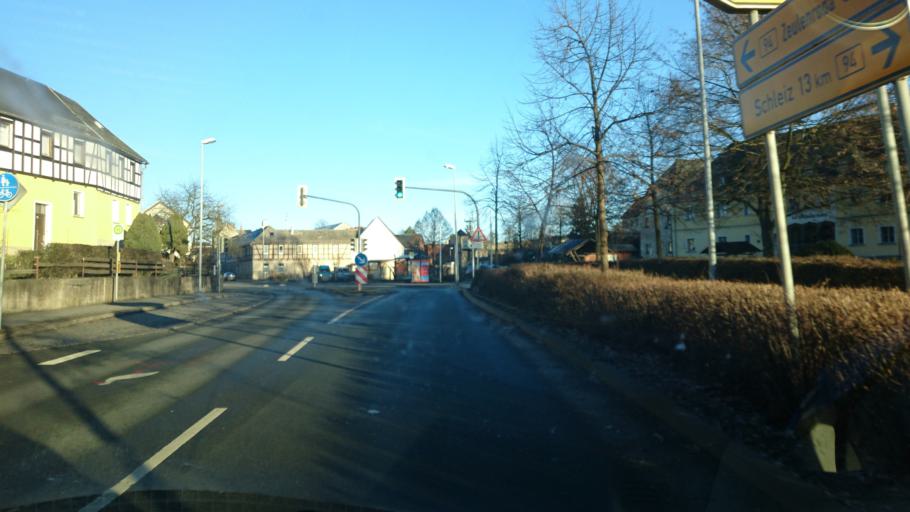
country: DE
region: Thuringia
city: Langenwolschendorf
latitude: 50.6347
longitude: 11.9538
